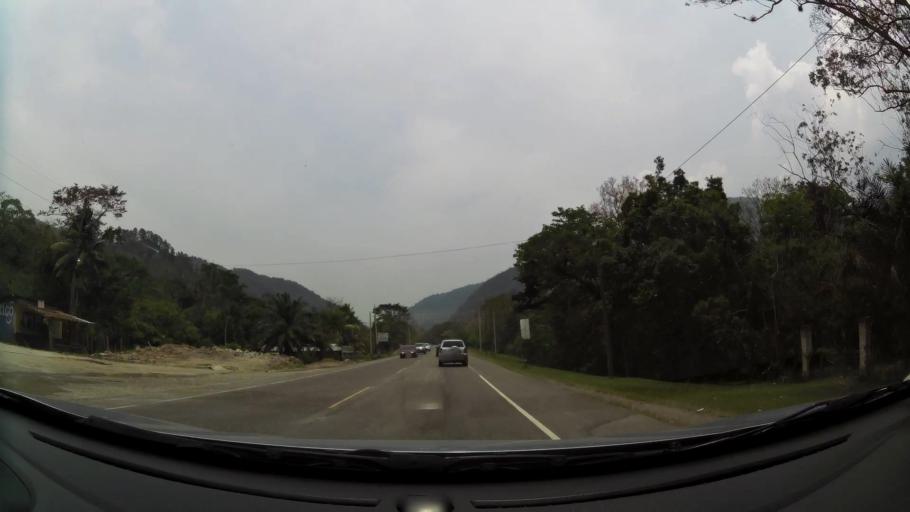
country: HN
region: Comayagua
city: Taulabe
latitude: 14.7177
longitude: -87.9654
